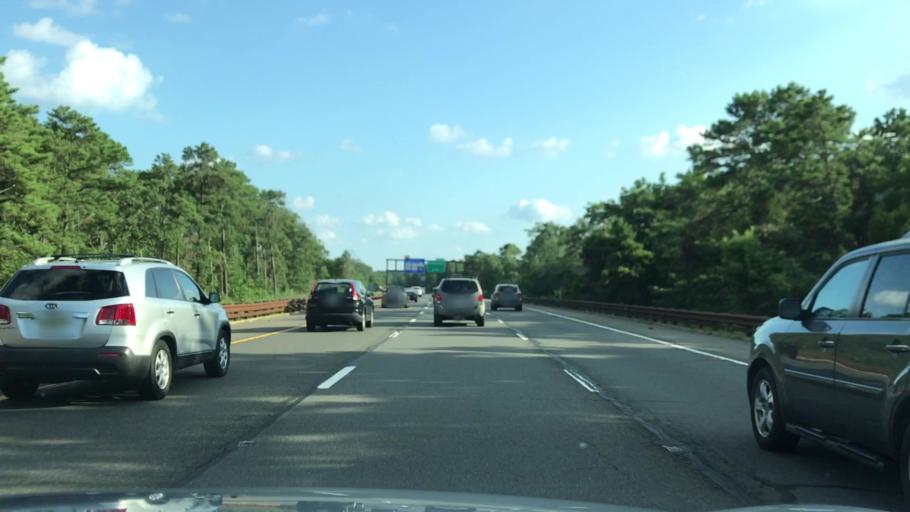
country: US
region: New Jersey
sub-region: Ocean County
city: South Toms River
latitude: 39.8922
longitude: -74.2129
